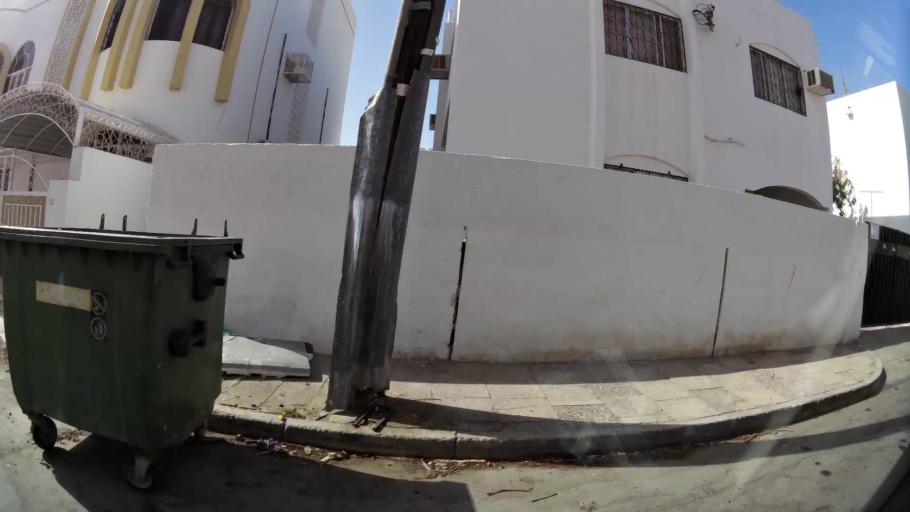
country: OM
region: Muhafazat Masqat
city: Muscat
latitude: 23.6010
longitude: 58.5128
